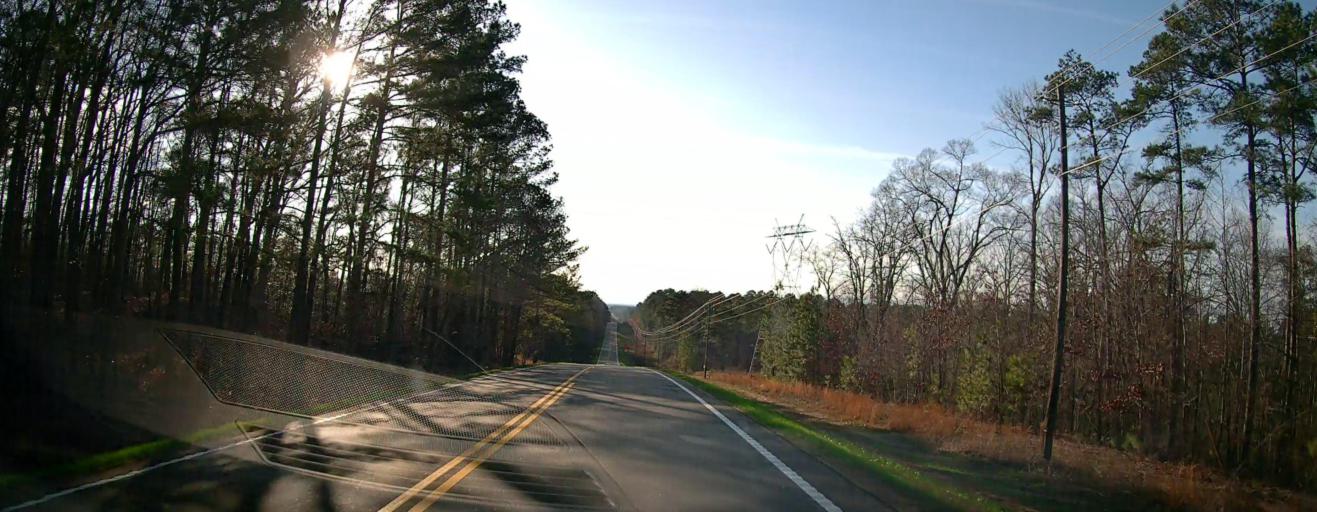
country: US
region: Georgia
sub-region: Harris County
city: Hamilton
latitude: 32.7472
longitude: -84.9839
